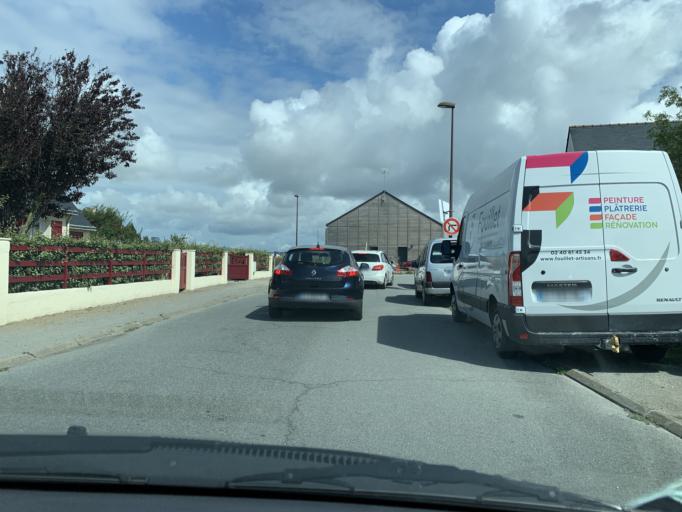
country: FR
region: Pays de la Loire
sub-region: Departement de la Loire-Atlantique
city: Le Pouliguen
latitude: 47.2959
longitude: -2.4350
